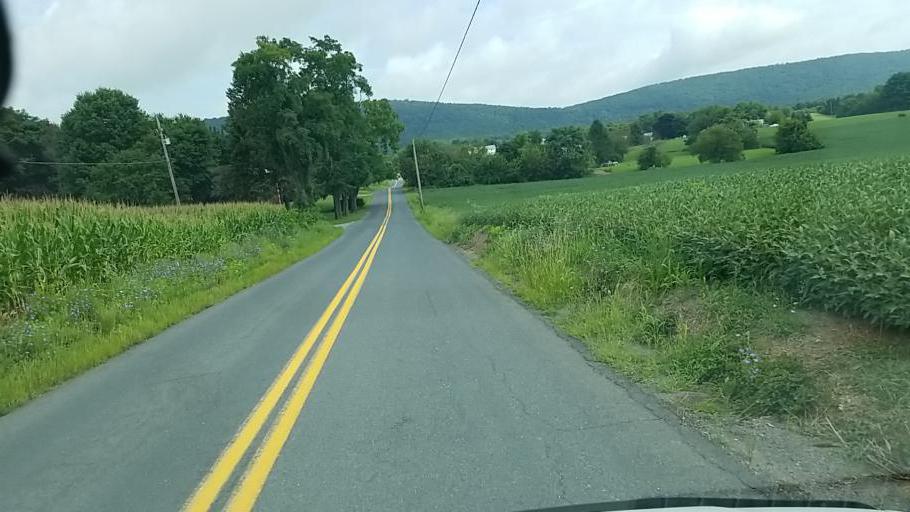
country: US
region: Pennsylvania
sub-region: Dauphin County
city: Millersburg
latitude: 40.5096
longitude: -76.8854
